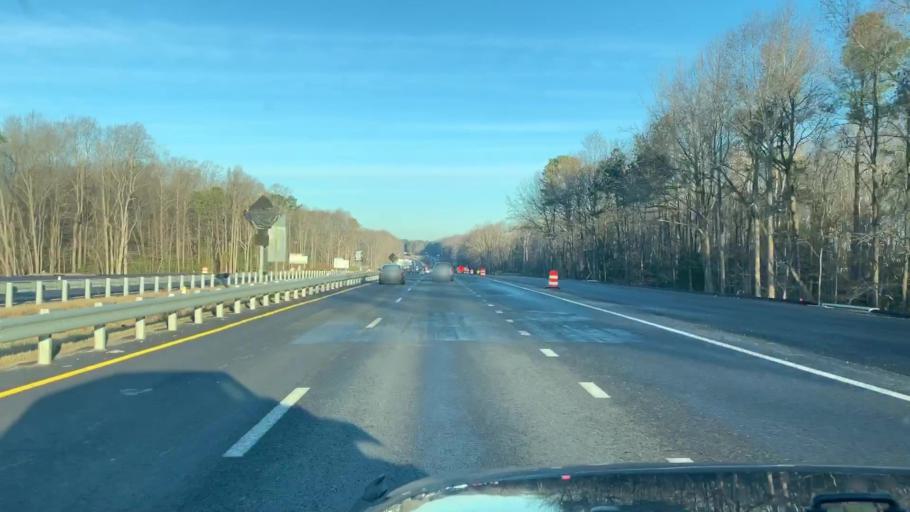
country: US
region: Virginia
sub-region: City of Williamsburg
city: Williamsburg
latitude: 37.2619
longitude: -76.6490
